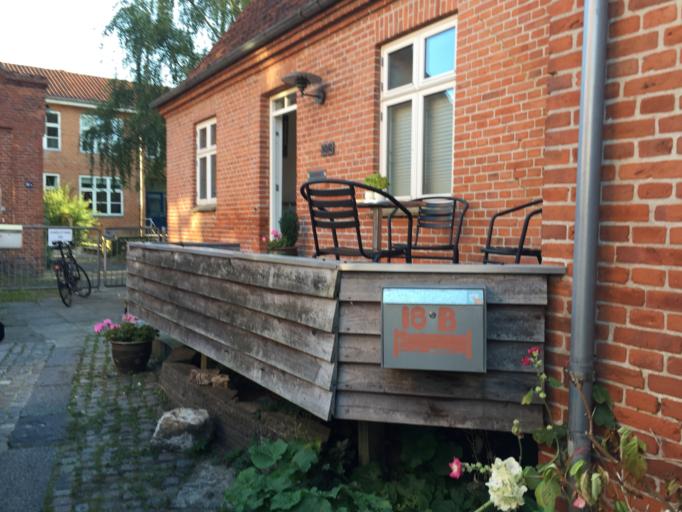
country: DK
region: Central Jutland
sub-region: Viborg Kommune
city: Viborg
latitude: 56.4520
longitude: 9.4123
